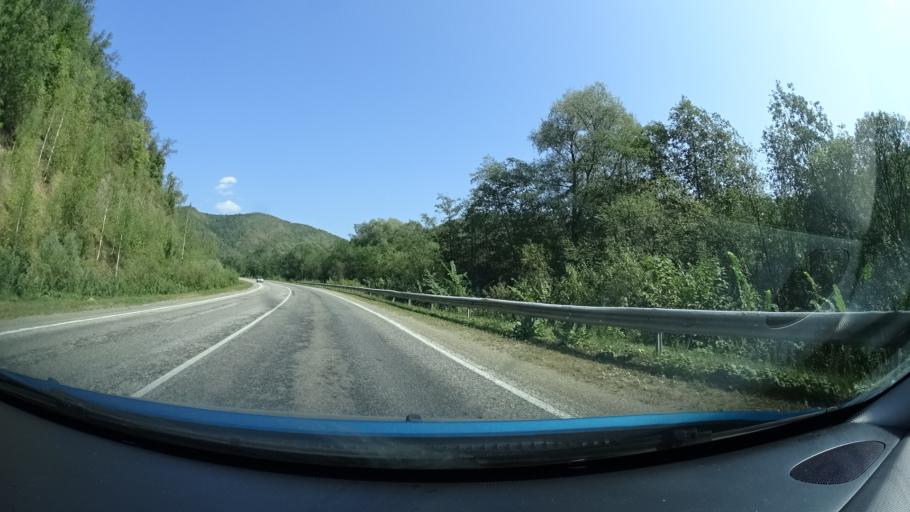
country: RU
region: Bashkortostan
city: Inzer
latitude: 54.3317
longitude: 57.1325
